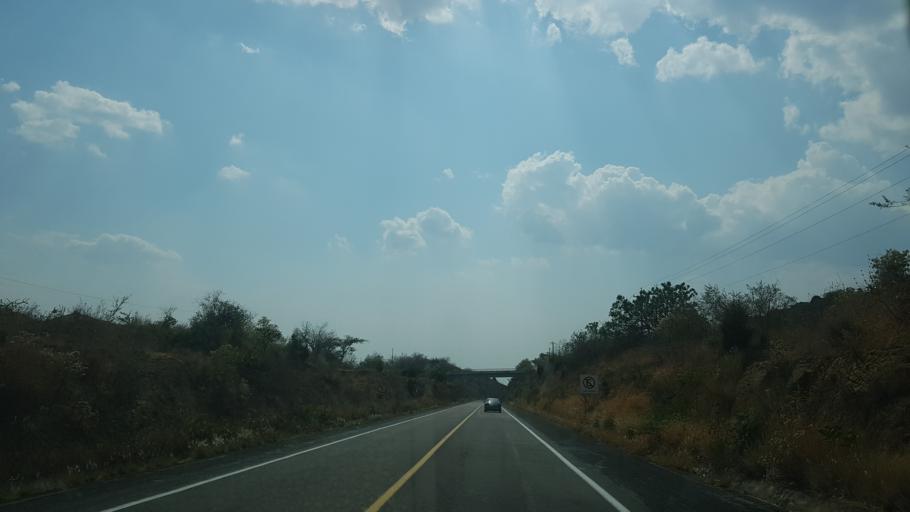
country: MX
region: Puebla
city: San Juan Amecac
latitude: 18.8159
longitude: -98.6691
